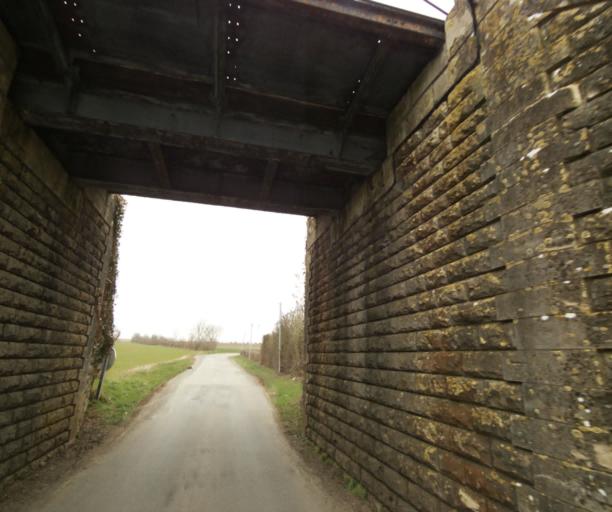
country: FR
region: Poitou-Charentes
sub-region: Departement des Deux-Sevres
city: Magne
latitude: 46.3311
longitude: -0.5294
